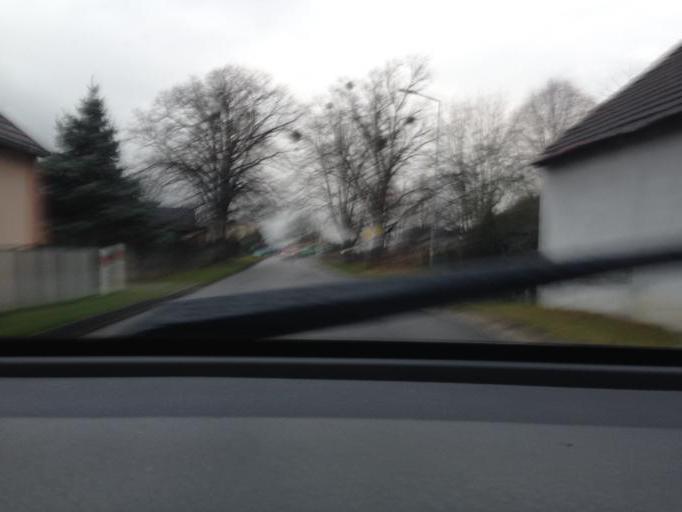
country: PL
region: Opole Voivodeship
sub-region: Powiat opolski
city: Wegry
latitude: 50.7306
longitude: 18.0473
